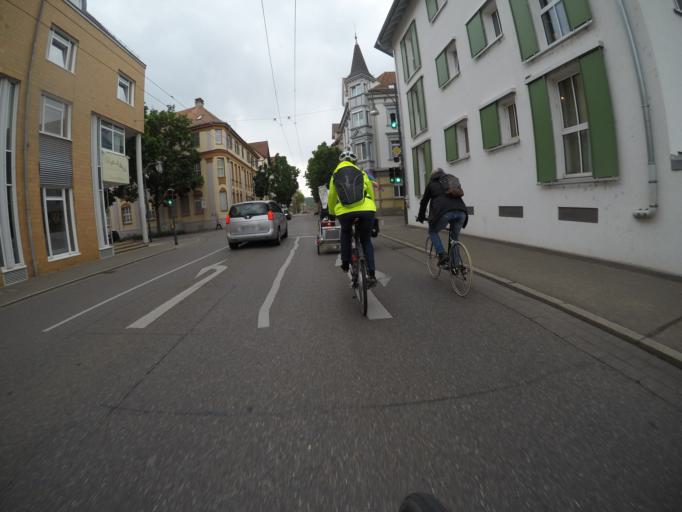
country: DE
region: Baden-Wuerttemberg
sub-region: Regierungsbezirk Stuttgart
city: Esslingen
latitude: 48.7368
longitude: 9.3140
